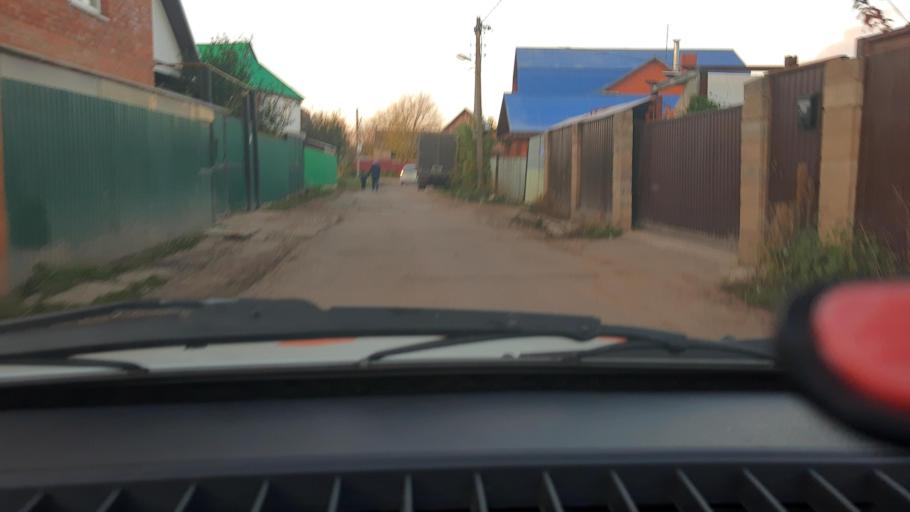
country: RU
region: Bashkortostan
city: Ufa
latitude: 54.7327
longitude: 55.9034
